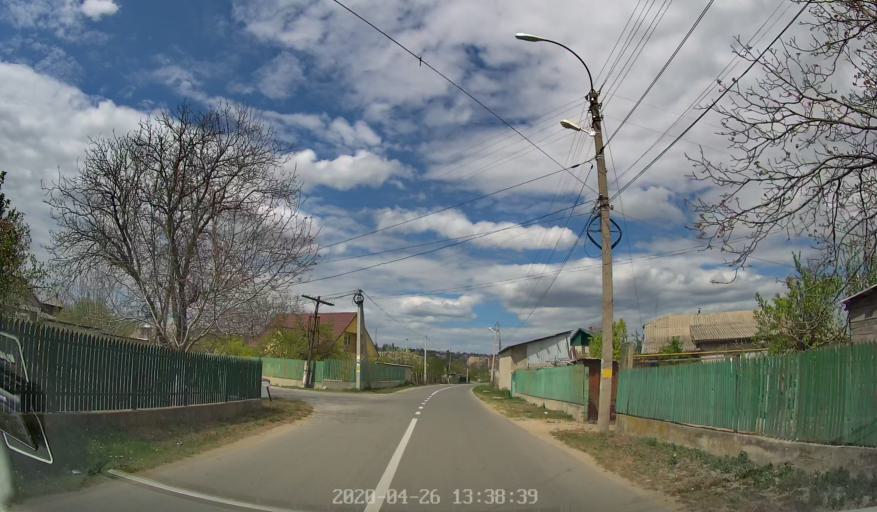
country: MD
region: Criuleni
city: Criuleni
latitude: 47.2093
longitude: 29.1657
